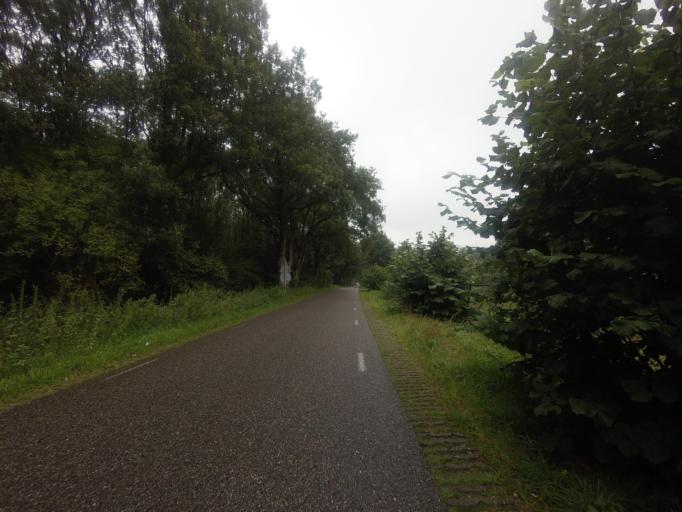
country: NL
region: Friesland
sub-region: Gemeente Heerenveen
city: Nieuwehorne
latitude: 52.9536
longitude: 6.0344
